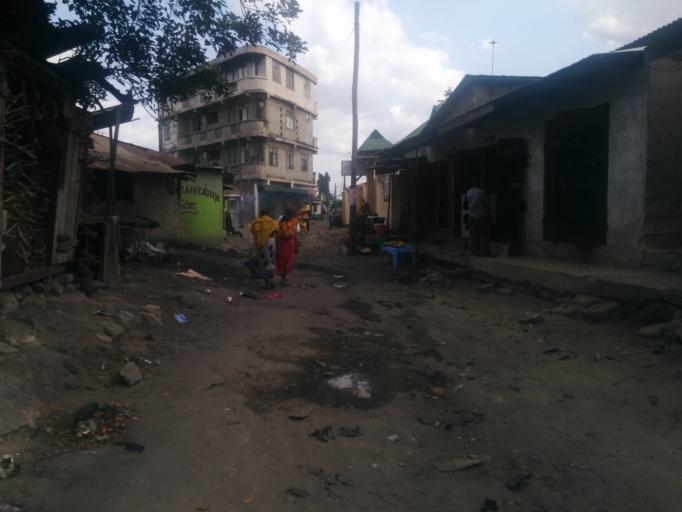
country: TZ
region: Dar es Salaam
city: Magomeni
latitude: -6.7981
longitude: 39.2360
